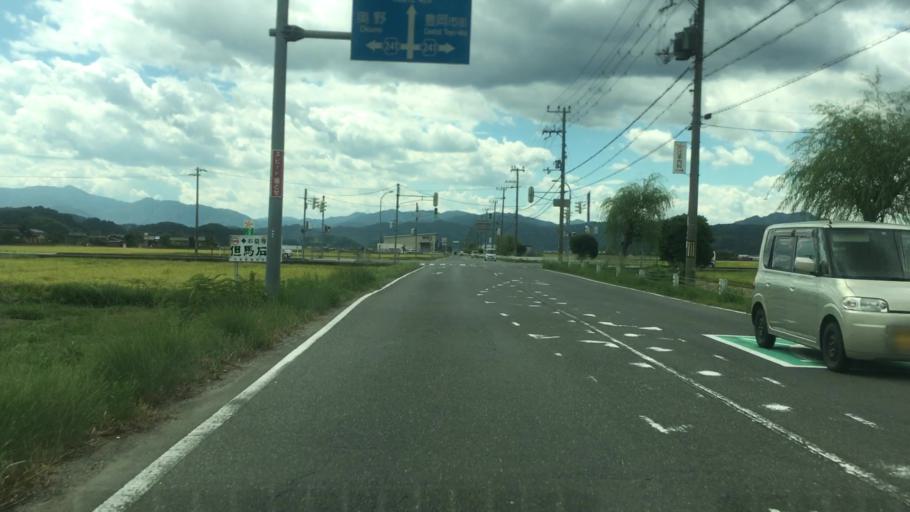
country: JP
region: Hyogo
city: Toyooka
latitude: 35.5286
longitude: 134.8398
